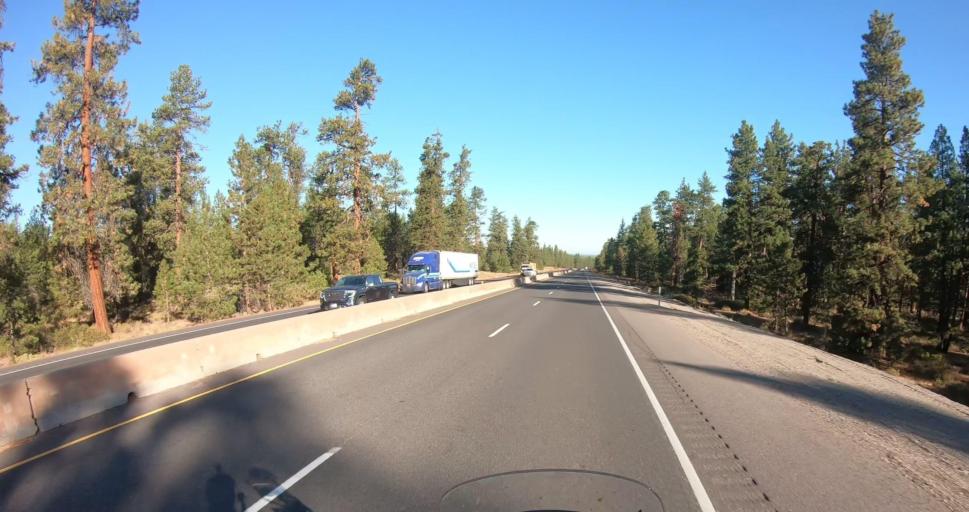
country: US
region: Oregon
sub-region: Deschutes County
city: Deschutes River Woods
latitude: 43.9201
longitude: -121.3500
